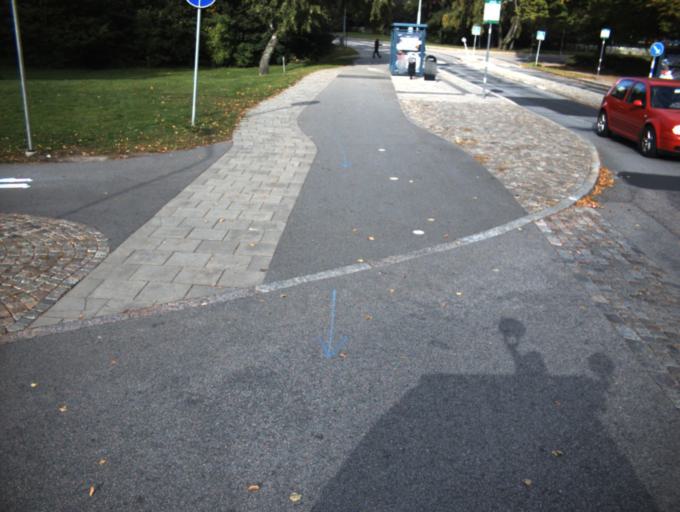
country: SE
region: Skane
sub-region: Helsingborg
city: Helsingborg
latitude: 56.0630
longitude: 12.6932
